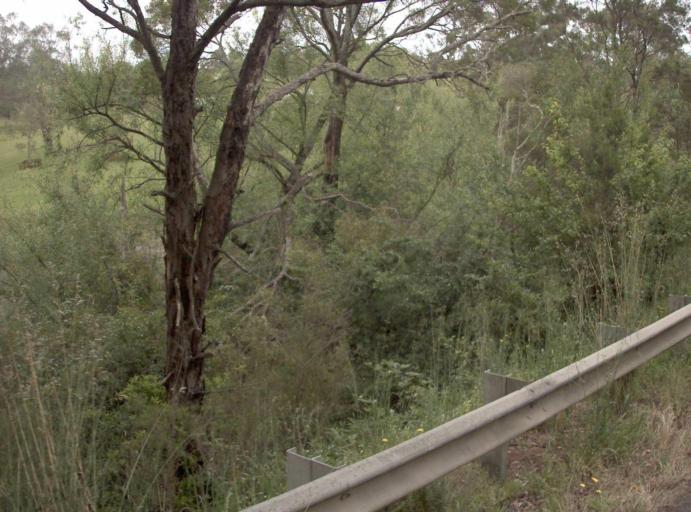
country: AU
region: Victoria
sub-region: Bass Coast
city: North Wonthaggi
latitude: -38.5579
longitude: 145.9509
